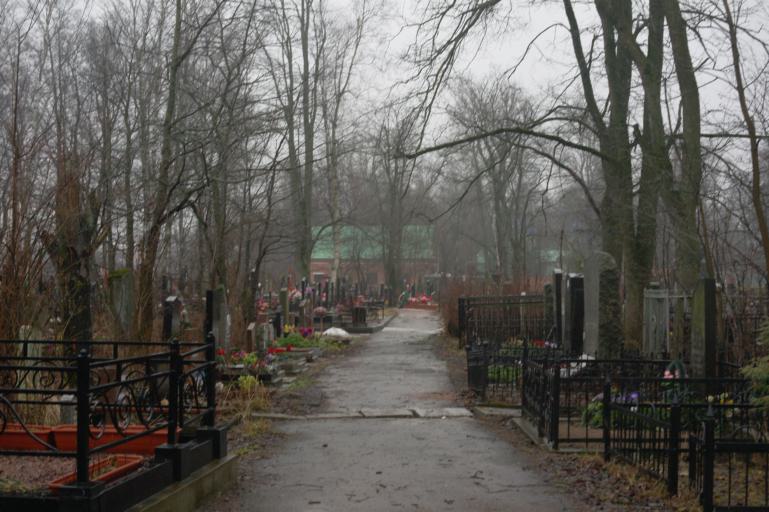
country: RU
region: St.-Petersburg
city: Komendantsky aerodrom
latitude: 59.9936
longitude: 30.2697
